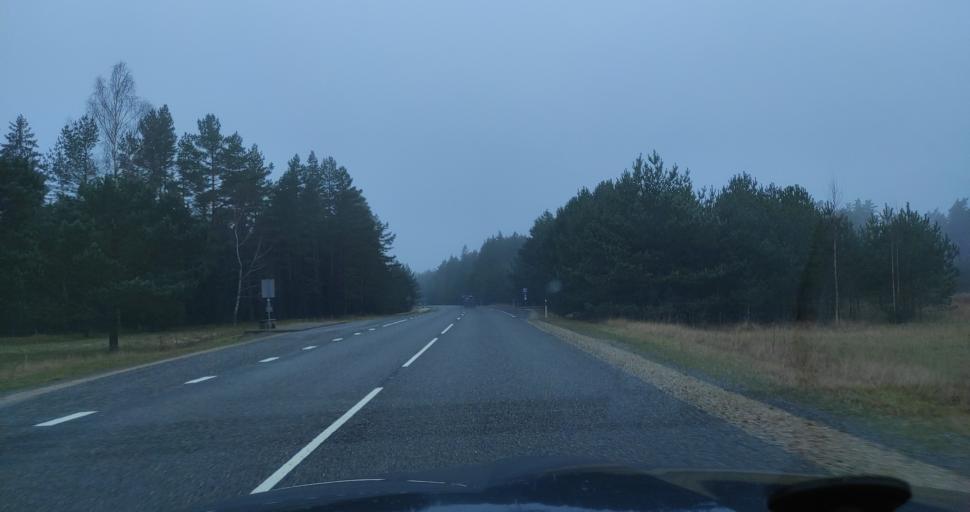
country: LV
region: Pavilostas
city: Pavilosta
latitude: 56.9711
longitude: 21.3456
